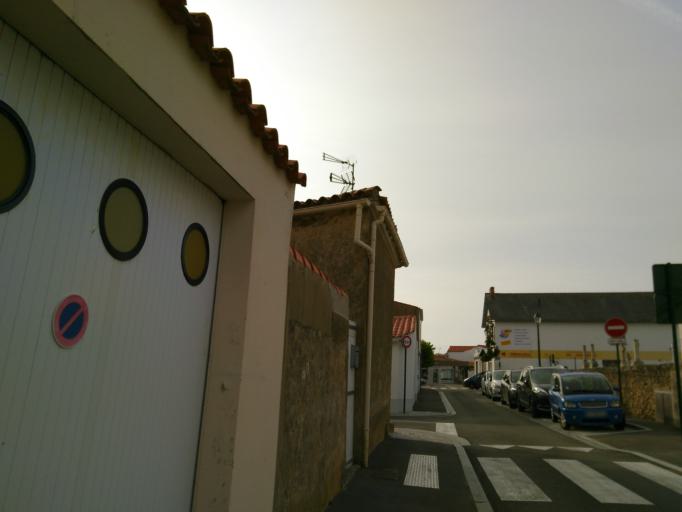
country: FR
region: Pays de la Loire
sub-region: Departement de la Vendee
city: Les Sables-d'Olonne
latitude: 46.4950
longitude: -1.8001
